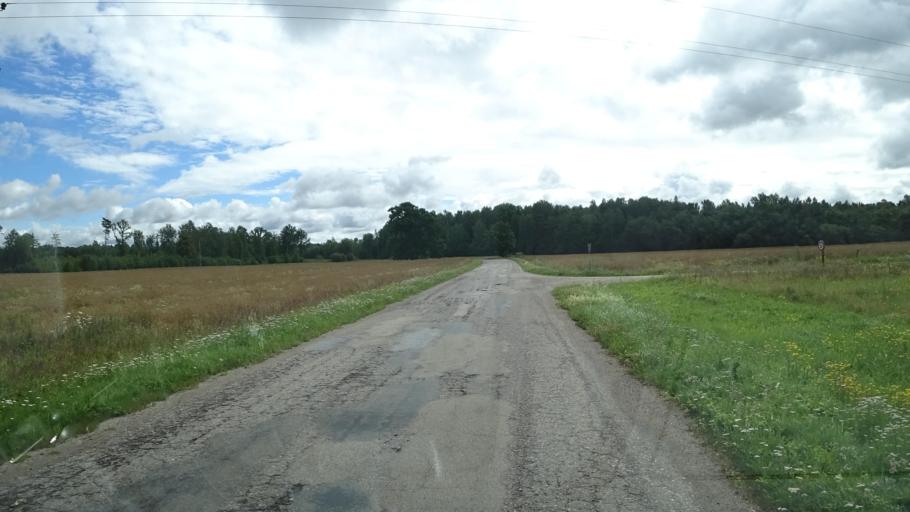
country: LV
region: Liepaja
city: Vec-Liepaja
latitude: 56.6575
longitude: 21.0890
